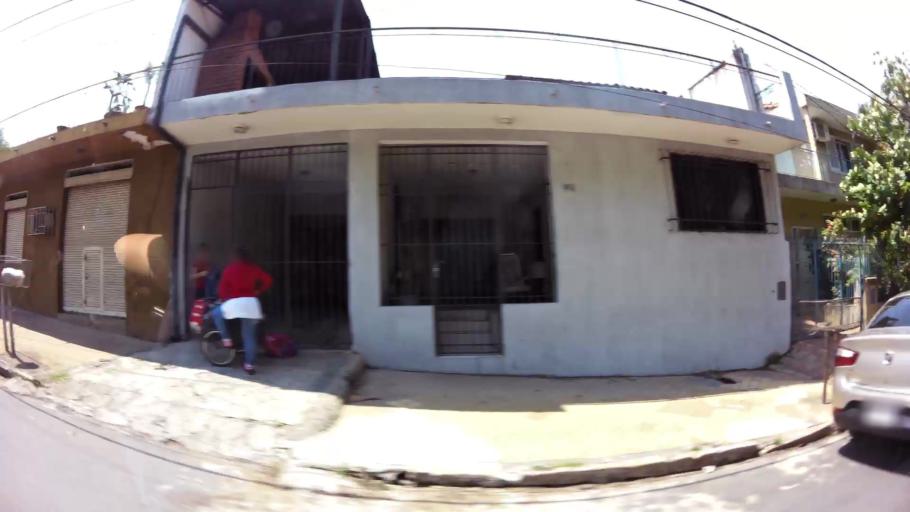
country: PY
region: Asuncion
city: Asuncion
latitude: -25.2941
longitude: -57.6503
